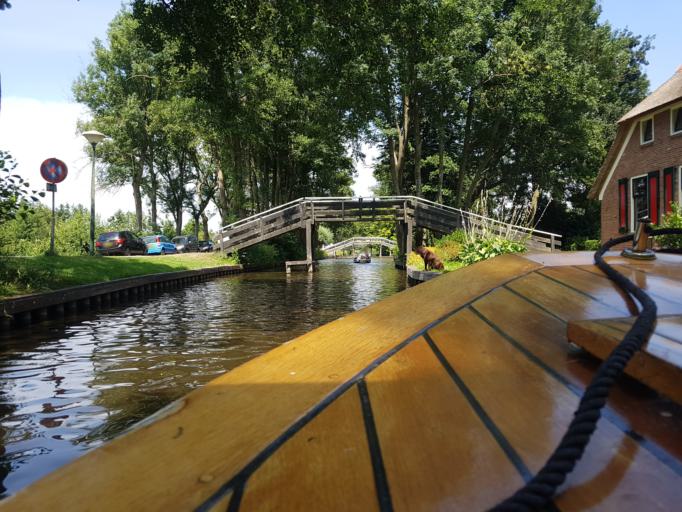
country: NL
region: Overijssel
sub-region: Gemeente Steenwijkerland
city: Giethoorn
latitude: 52.7300
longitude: 6.0910
